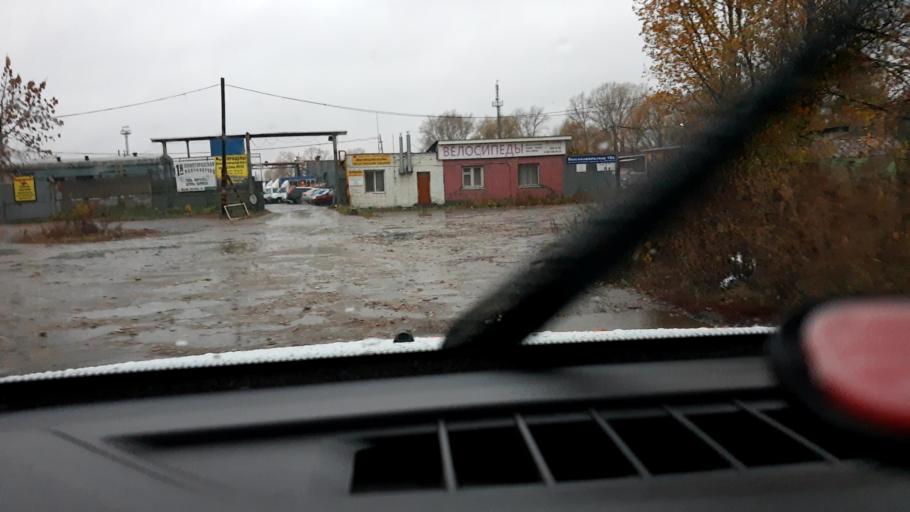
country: RU
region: Nizjnij Novgorod
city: Nizhniy Novgorod
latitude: 56.3103
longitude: 43.8797
